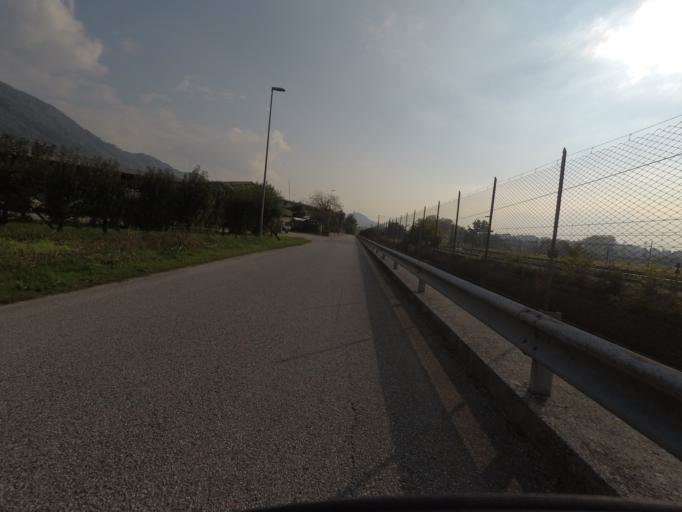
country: IT
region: Friuli Venezia Giulia
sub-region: Provincia di Udine
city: Artegna
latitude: 46.2322
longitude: 13.1577
